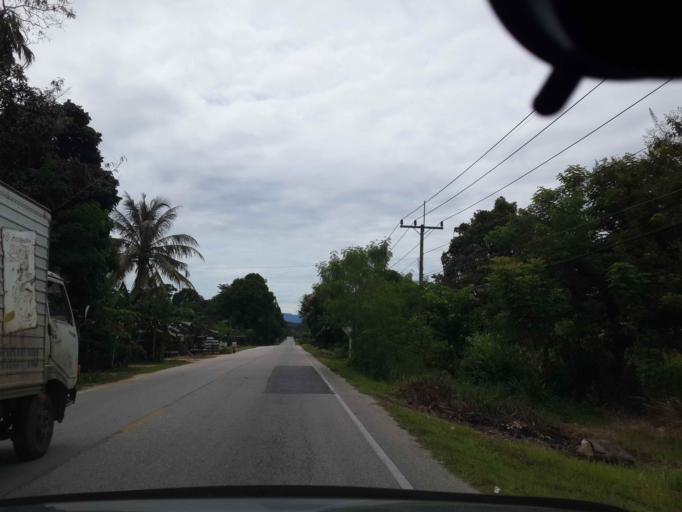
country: TH
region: Narathiwat
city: Yi-ngo
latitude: 6.3516
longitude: 101.6192
